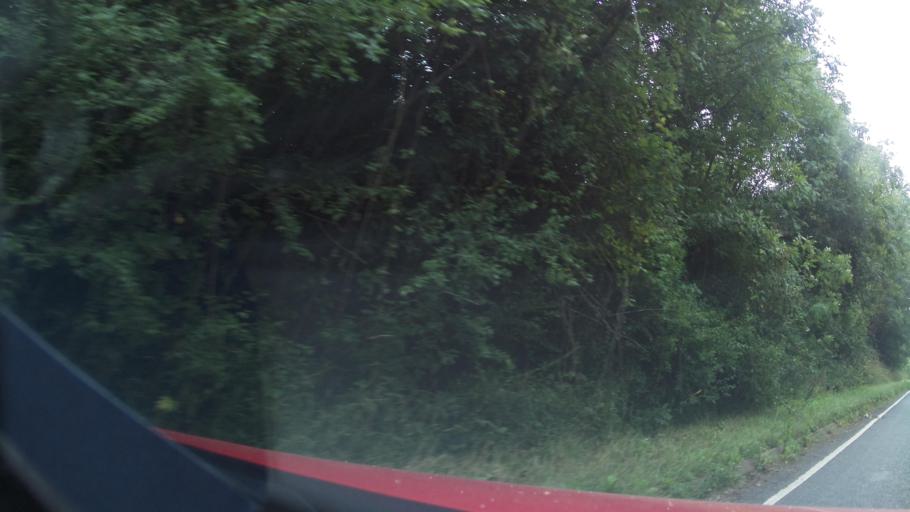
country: GB
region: England
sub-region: Dorset
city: Stalbridge
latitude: 50.9866
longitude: -2.4063
